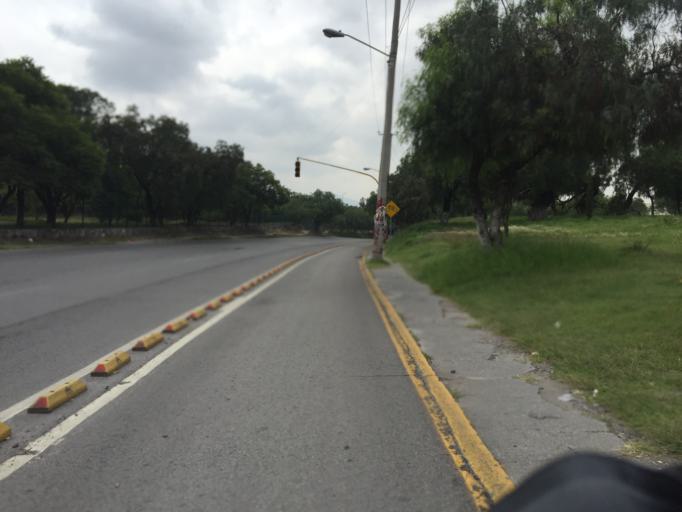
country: MX
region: Mexico
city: Cuautitlan Izcalli
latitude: 19.6560
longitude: -99.2058
